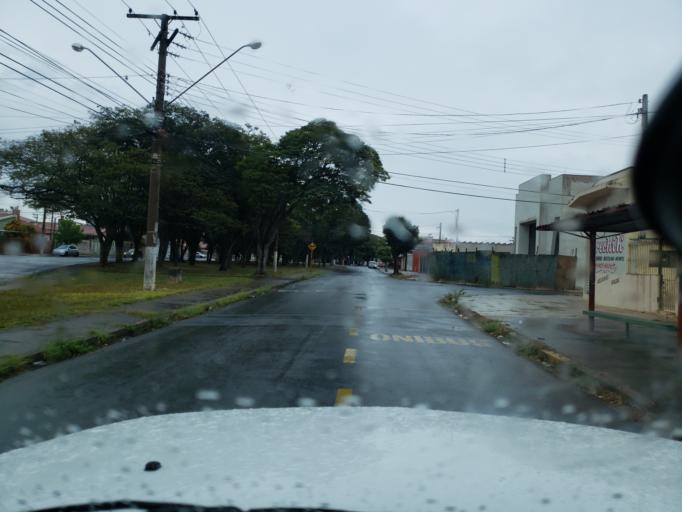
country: BR
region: Sao Paulo
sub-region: Moji-Guacu
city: Mogi-Gaucu
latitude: -22.3543
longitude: -46.9436
